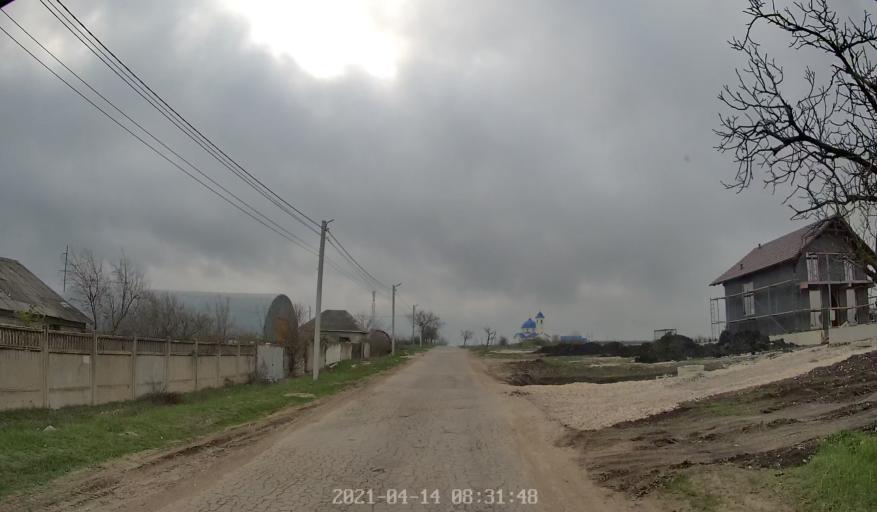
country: MD
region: Chisinau
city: Stauceni
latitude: 47.0605
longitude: 28.9367
